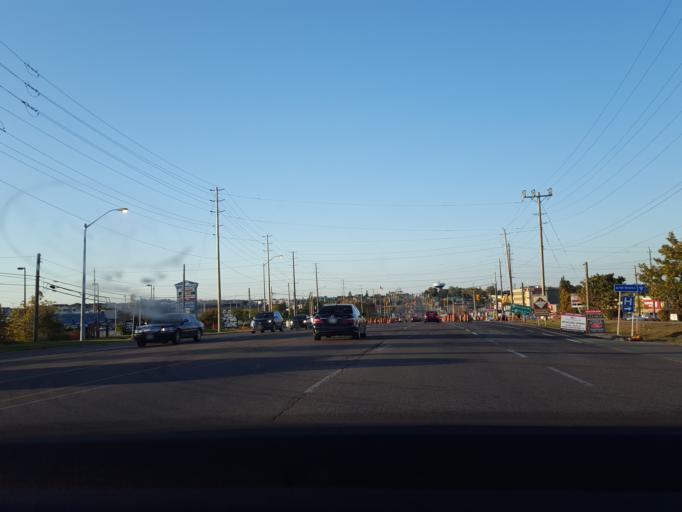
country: CA
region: Ontario
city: Newmarket
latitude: 44.0530
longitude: -79.4798
